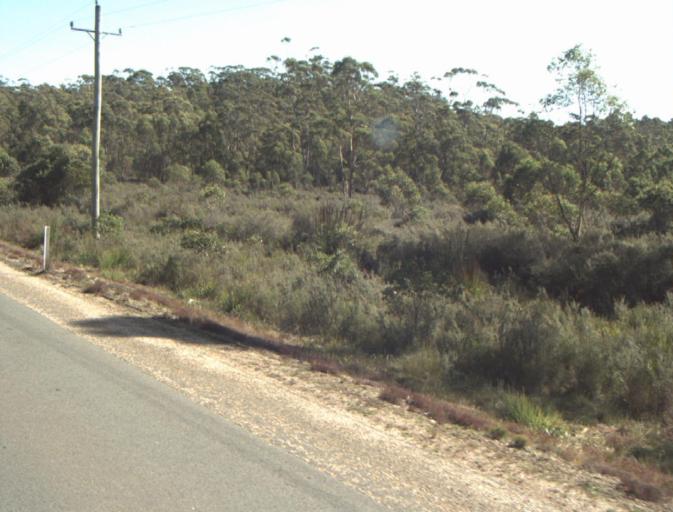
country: AU
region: Tasmania
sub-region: Launceston
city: Mayfield
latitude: -41.3147
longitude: 147.1957
